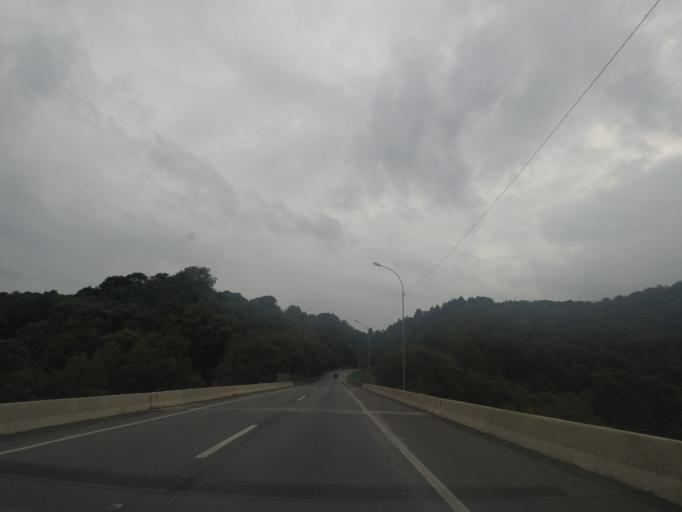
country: BR
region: Parana
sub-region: Campina Grande Do Sul
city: Campina Grande do Sul
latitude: -25.1803
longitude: -48.8813
